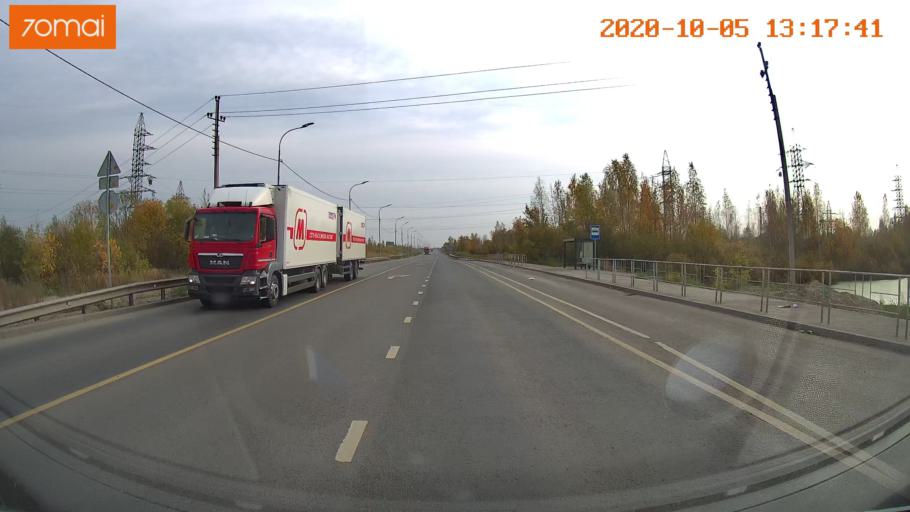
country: RU
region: Ivanovo
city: Novo-Talitsy
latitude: 56.9842
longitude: 40.9120
